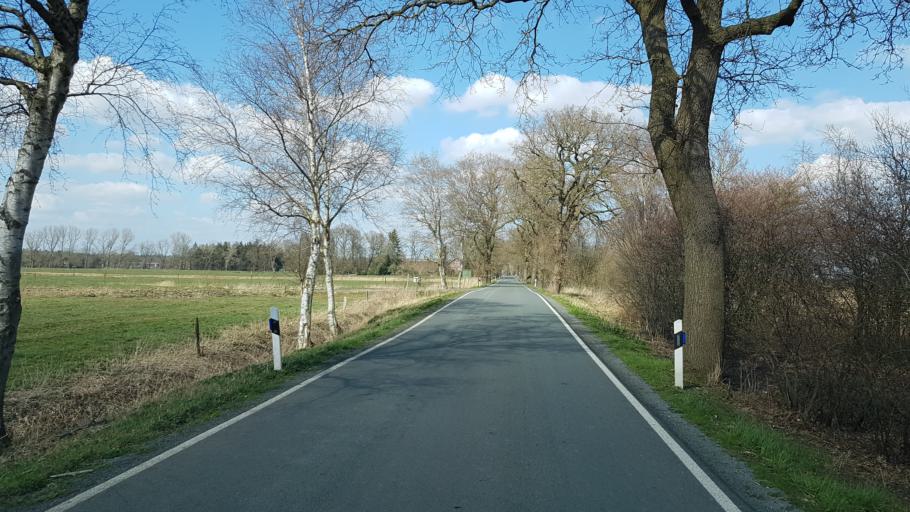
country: DE
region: Lower Saxony
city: Rastede
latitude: 53.3184
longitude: 8.2289
